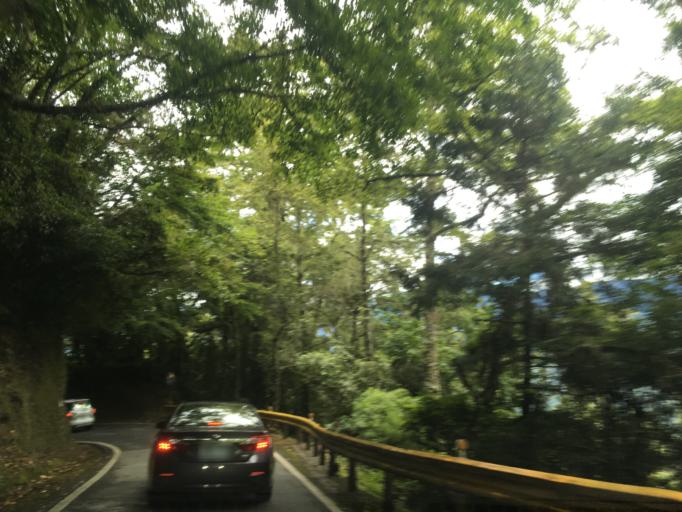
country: TW
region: Taiwan
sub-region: Hualien
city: Hualian
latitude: 24.1753
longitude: 121.3833
